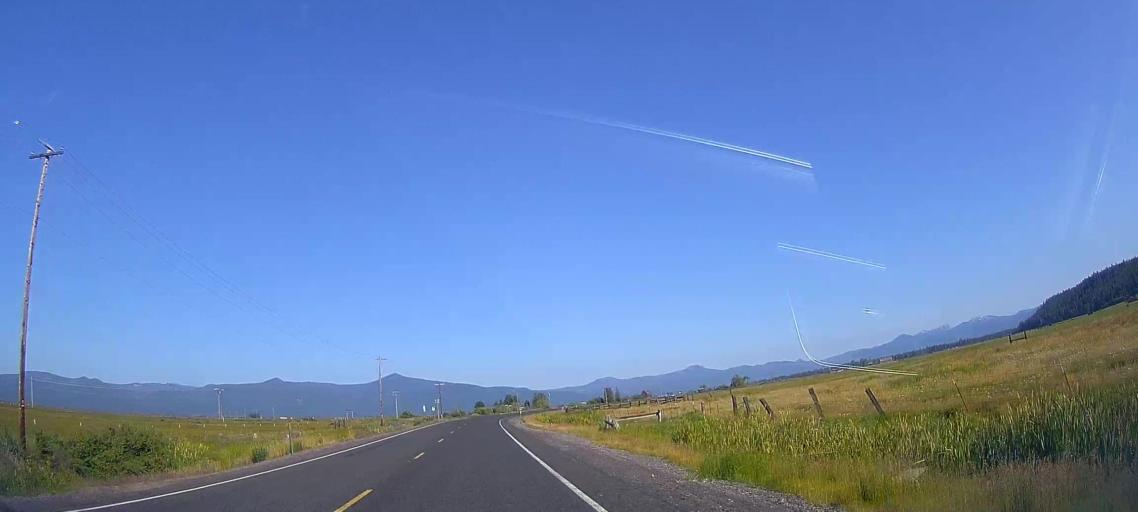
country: US
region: Oregon
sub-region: Klamath County
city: Klamath Falls
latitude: 42.6459
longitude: -121.9507
